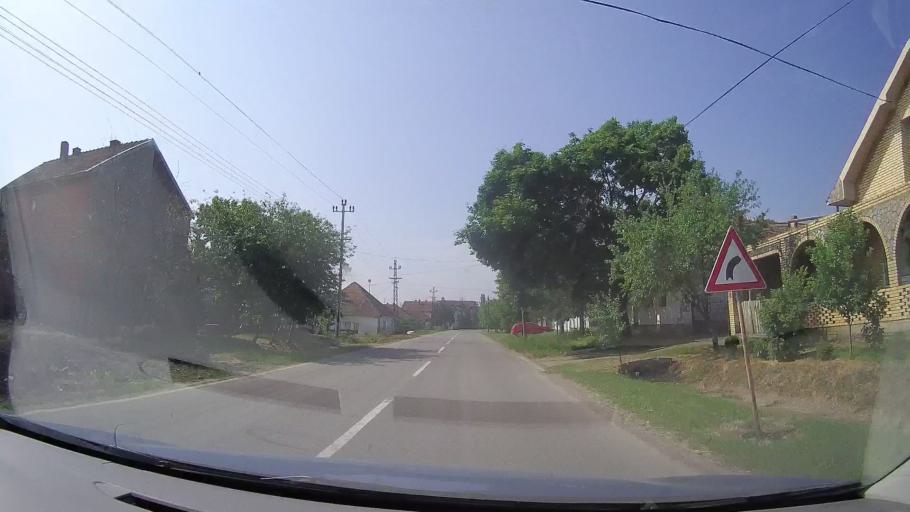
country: RS
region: Autonomna Pokrajina Vojvodina
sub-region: Srednjebanatski Okrug
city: Secanj
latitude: 45.3691
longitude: 20.7771
